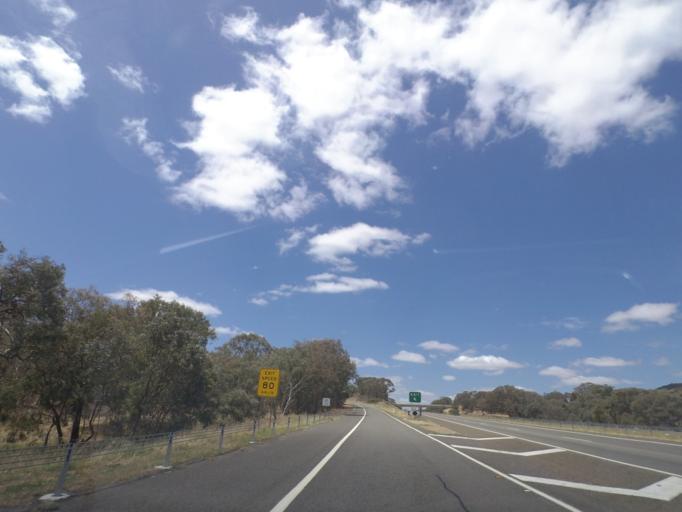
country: AU
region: Victoria
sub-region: Wangaratta
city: Wangaratta
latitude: -36.4688
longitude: 146.2054
